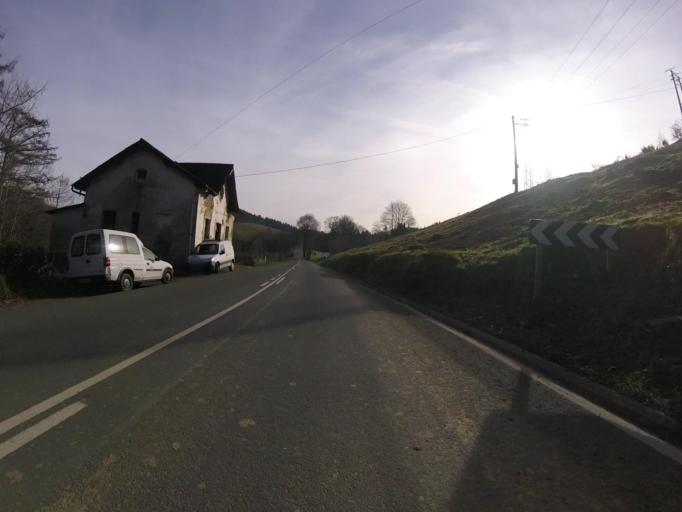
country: ES
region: Basque Country
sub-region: Provincia de Guipuzcoa
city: Berastegui
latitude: 43.1062
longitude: -1.9623
